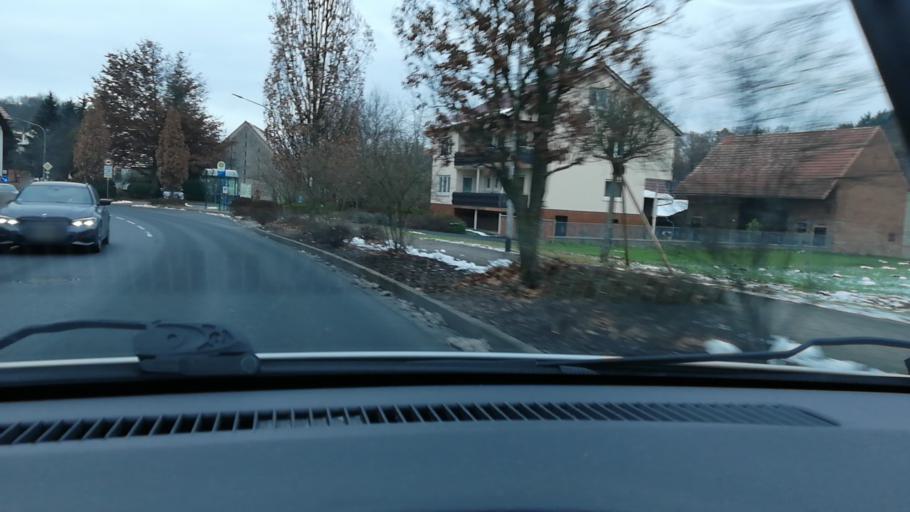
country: DE
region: Bavaria
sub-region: Regierungsbezirk Unterfranken
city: Schollkrippen
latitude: 50.0939
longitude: 9.2412
